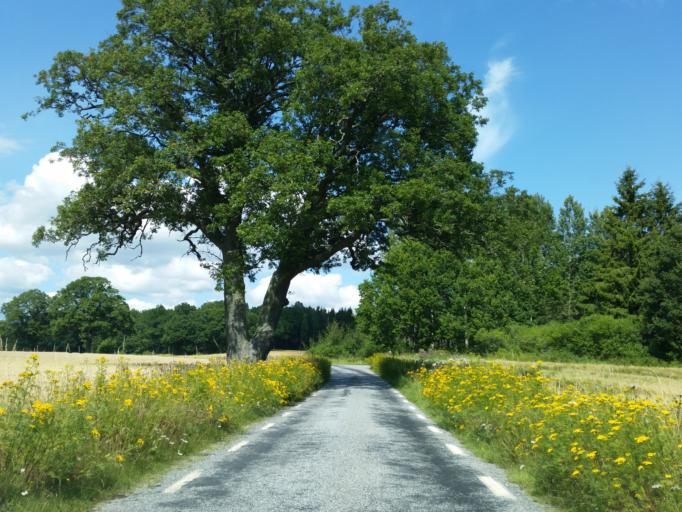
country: SE
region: Stockholm
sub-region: Sodertalje Kommun
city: Pershagen
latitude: 59.0504
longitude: 17.6596
